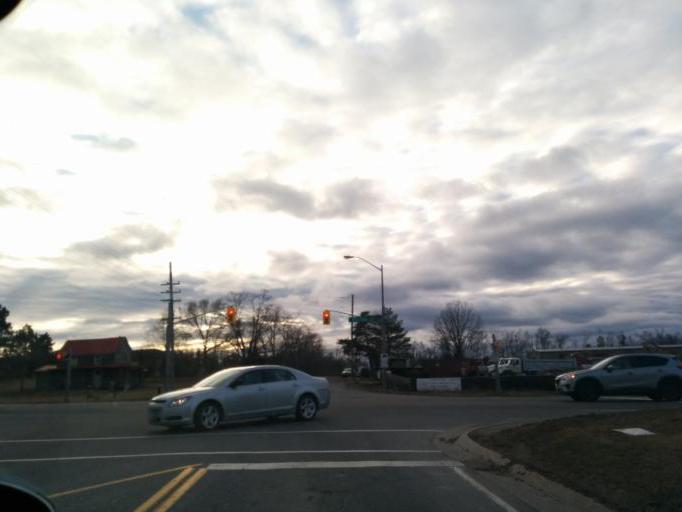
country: CA
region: Ontario
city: Bradford West Gwillimbury
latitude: 43.9929
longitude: -79.6740
